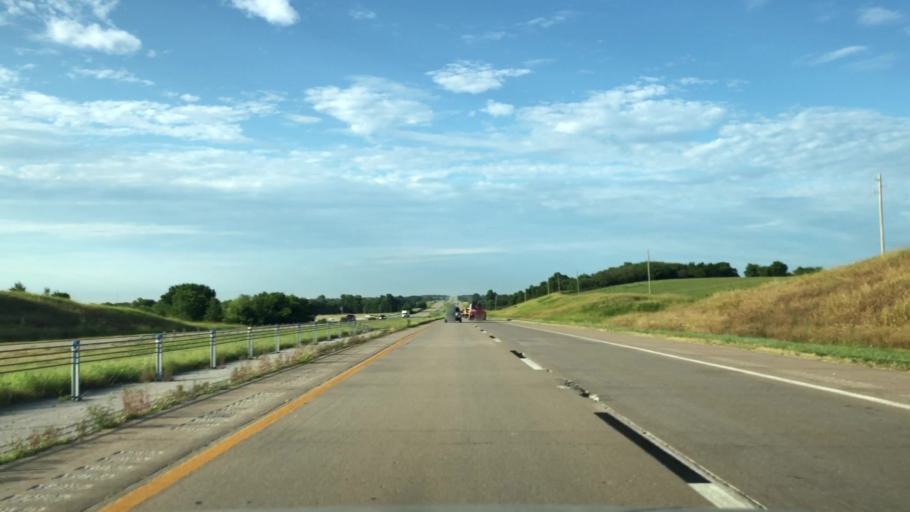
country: US
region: Oklahoma
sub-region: Osage County
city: Skiatook
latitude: 36.4779
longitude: -95.9207
